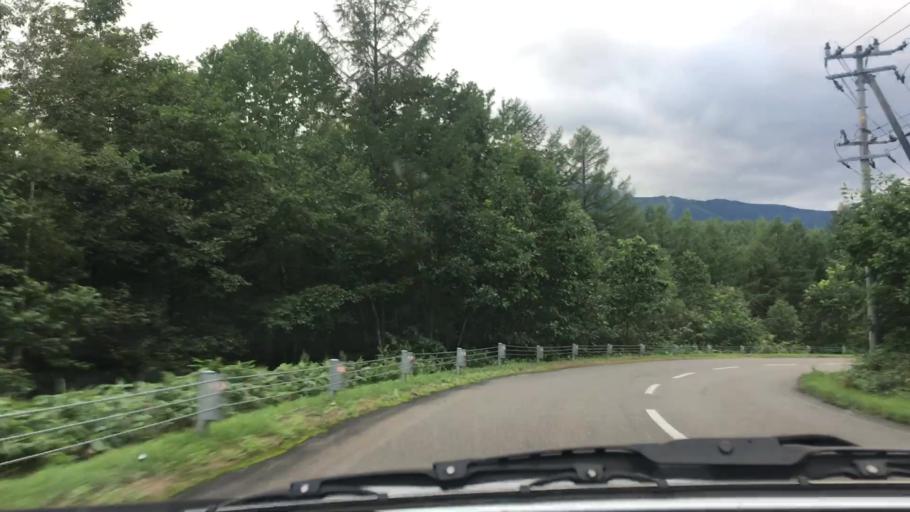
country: JP
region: Hokkaido
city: Otofuke
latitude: 43.1529
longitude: 142.8590
